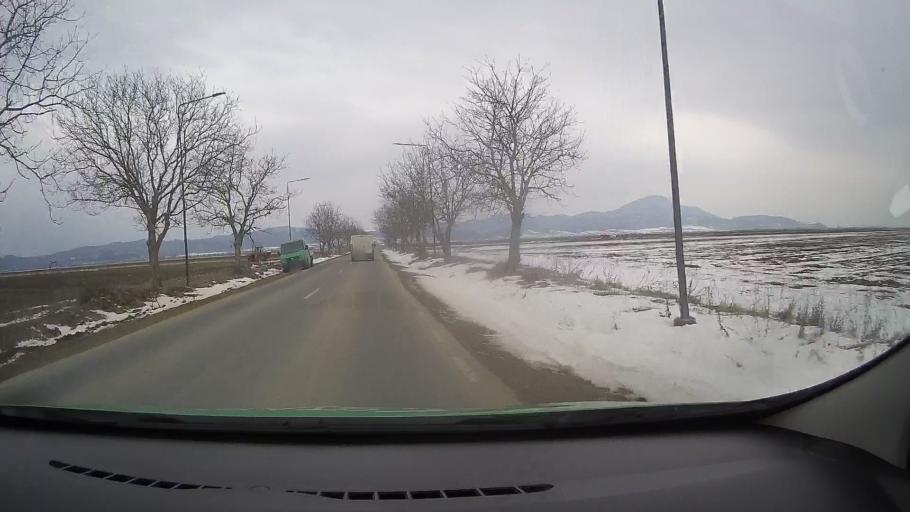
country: RO
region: Brasov
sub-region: Comuna Cristian
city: Cristian
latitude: 45.6307
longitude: 25.4629
